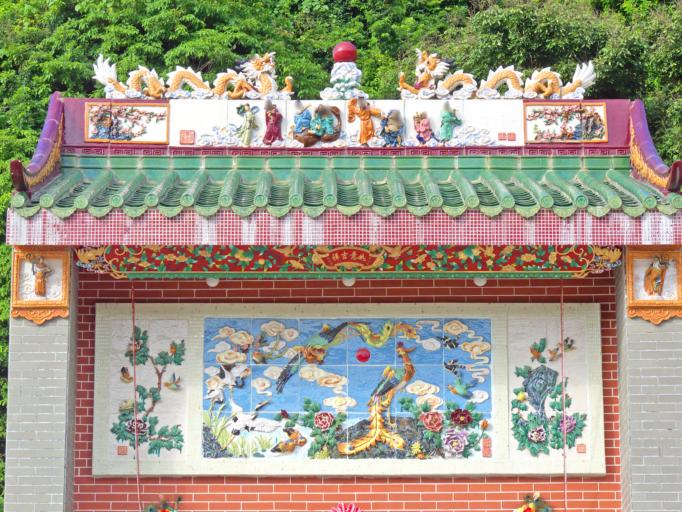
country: HK
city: Sok Kwu Wan
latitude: 22.2039
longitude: 114.1311
